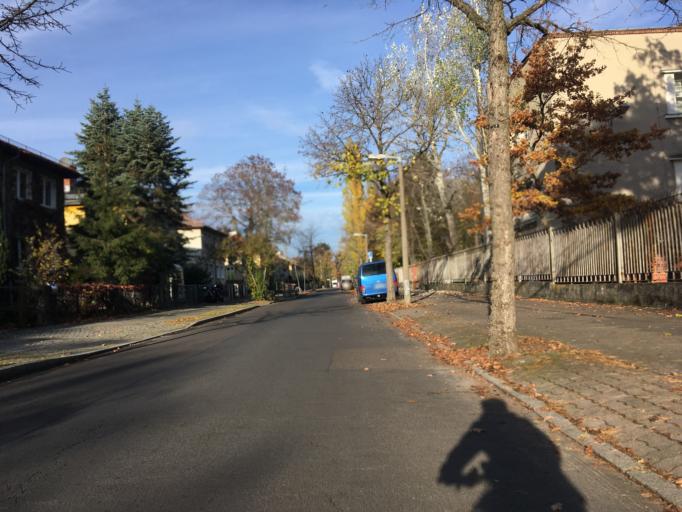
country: DE
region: Berlin
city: Karlshorst
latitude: 52.4881
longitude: 13.5329
